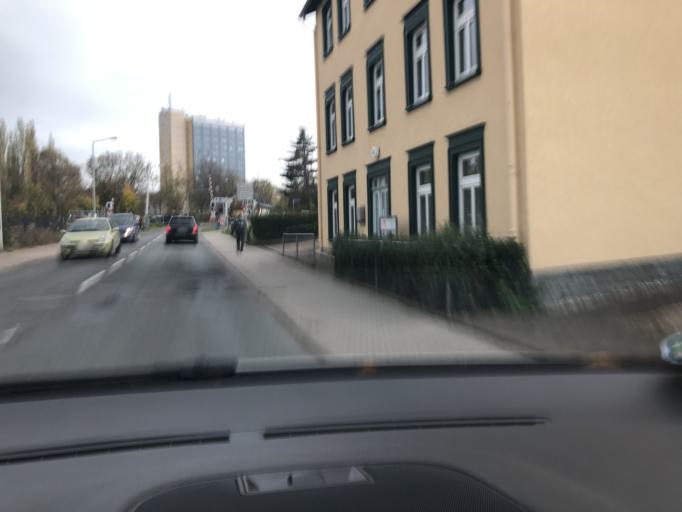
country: DE
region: Thuringia
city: Ilmenau
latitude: 50.6808
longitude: 10.9179
